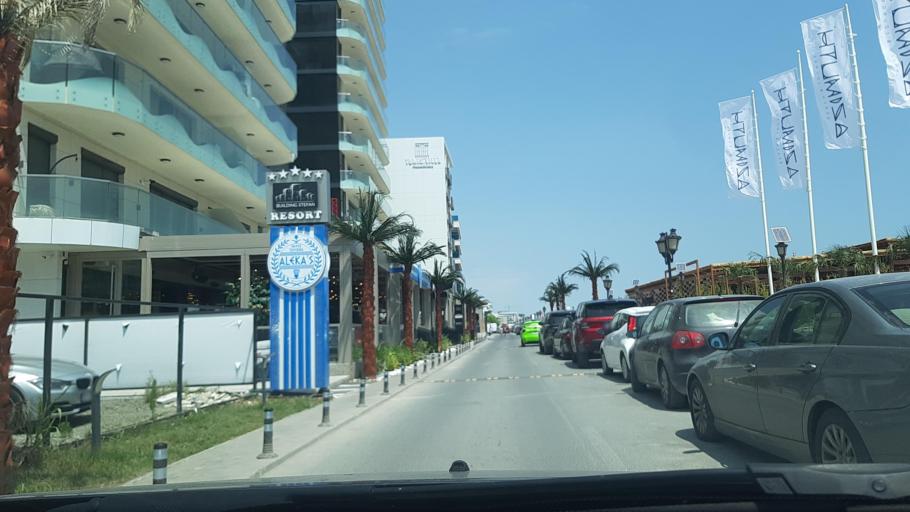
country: RO
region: Constanta
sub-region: Comuna Navodari
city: Navodari
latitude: 44.2937
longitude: 28.6241
